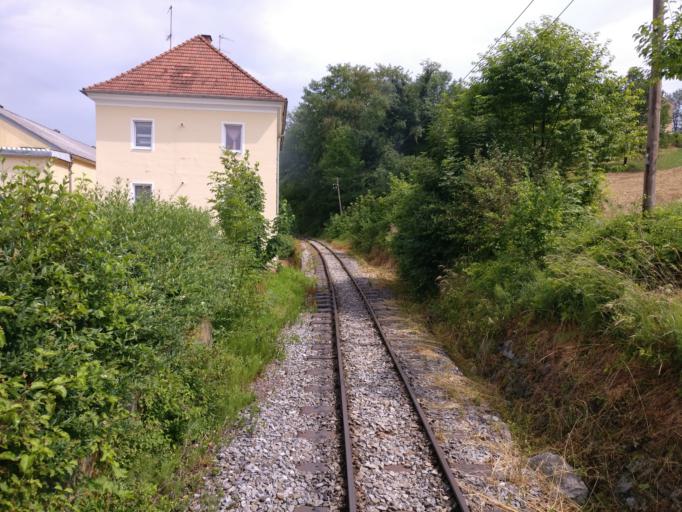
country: AT
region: Upper Austria
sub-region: Politischer Bezirk Steyr-Land
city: Sierning
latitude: 48.0325
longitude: 14.3378
